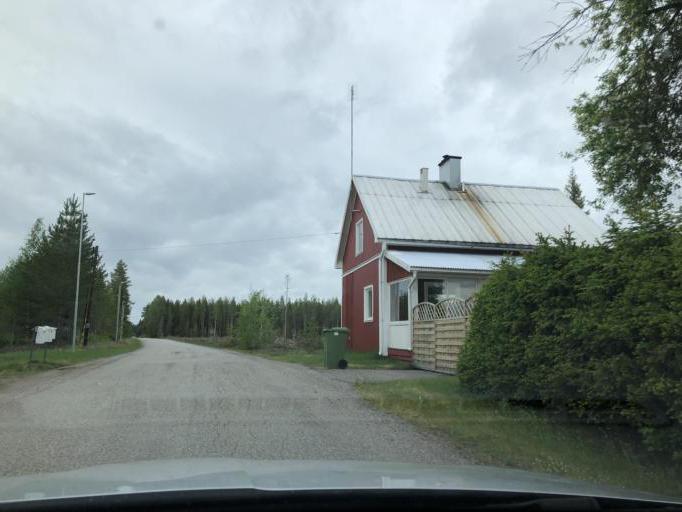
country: SE
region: Norrbotten
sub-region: Pitea Kommun
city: Roknas
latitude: 65.3782
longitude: 21.2776
